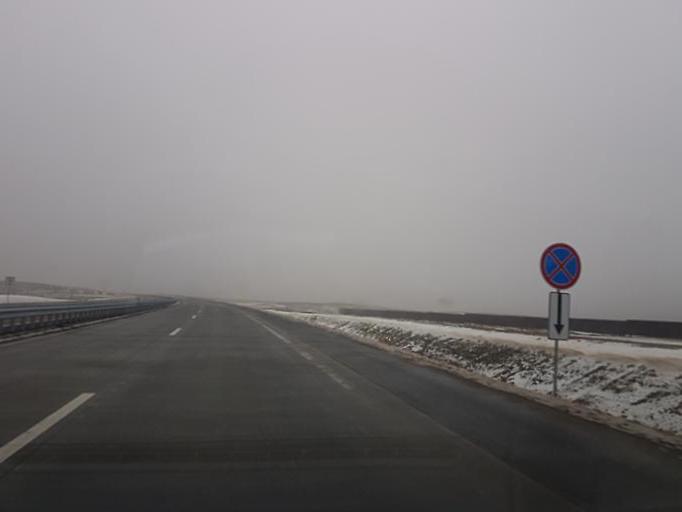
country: BY
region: Minsk
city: Atolina
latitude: 53.7578
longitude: 27.4061
